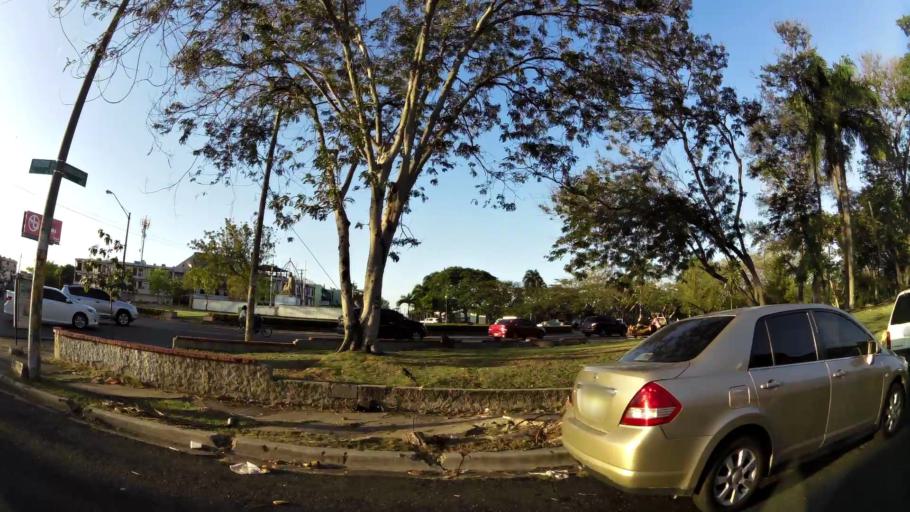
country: DO
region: Nacional
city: La Agustina
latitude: 18.4876
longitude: -69.9591
